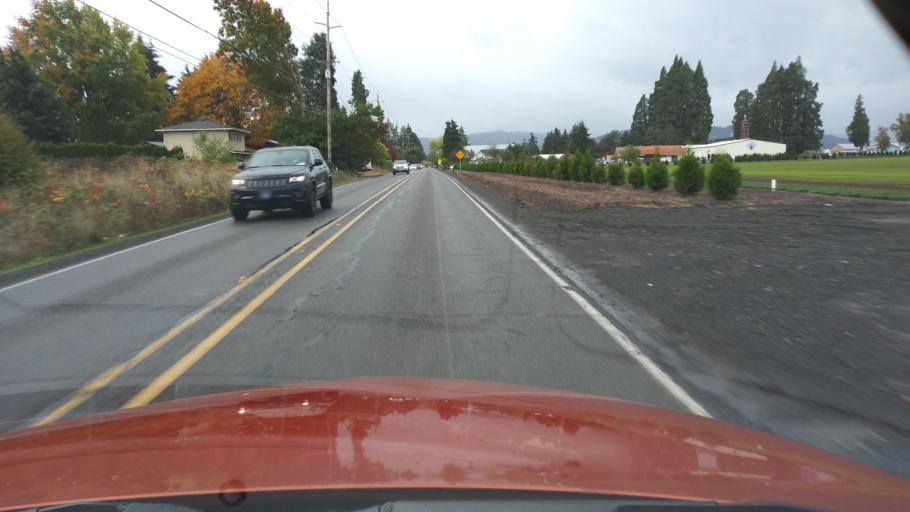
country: US
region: Oregon
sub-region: Washington County
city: Cornelius
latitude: 45.5507
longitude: -123.0799
